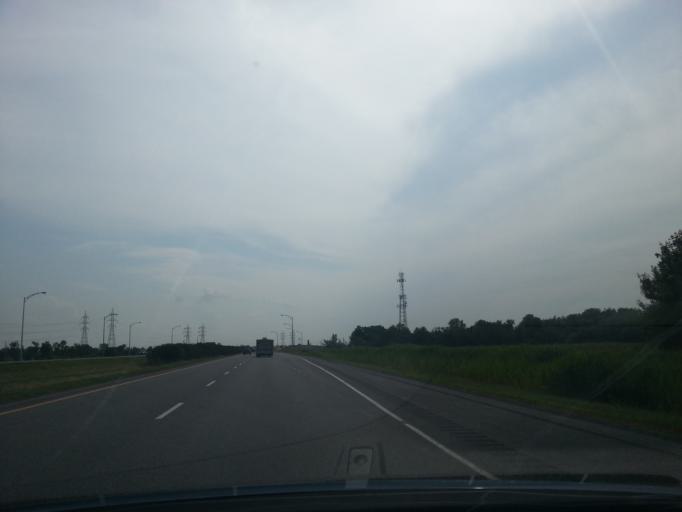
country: CA
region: Quebec
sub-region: Monteregie
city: Saint-Constant
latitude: 45.3573
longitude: -73.6405
